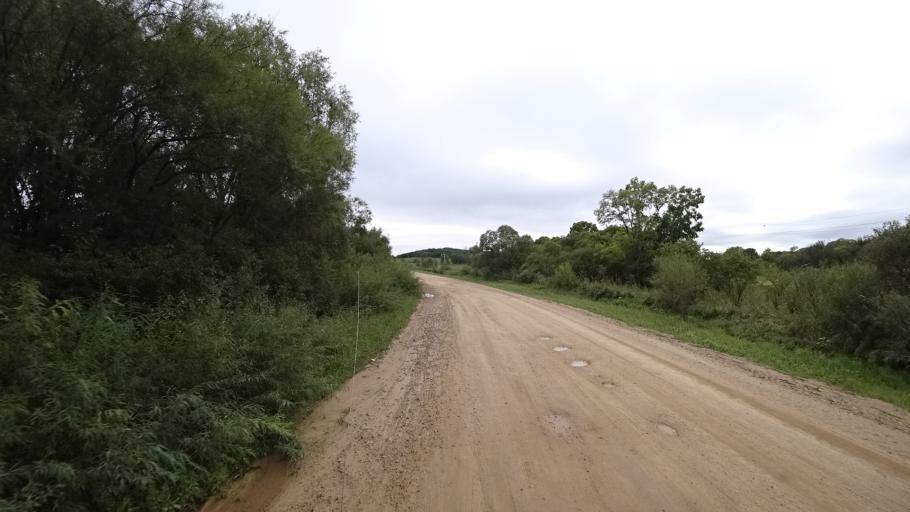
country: RU
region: Primorskiy
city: Monastyrishche
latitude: 44.0991
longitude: 132.6027
